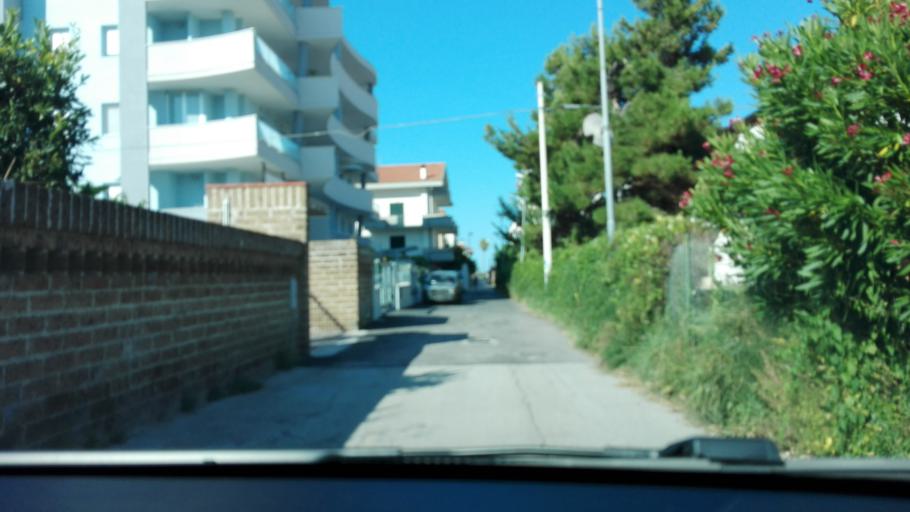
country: IT
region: Abruzzo
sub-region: Provincia di Pescara
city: Montesilvano Marina
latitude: 42.5107
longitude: 14.1650
